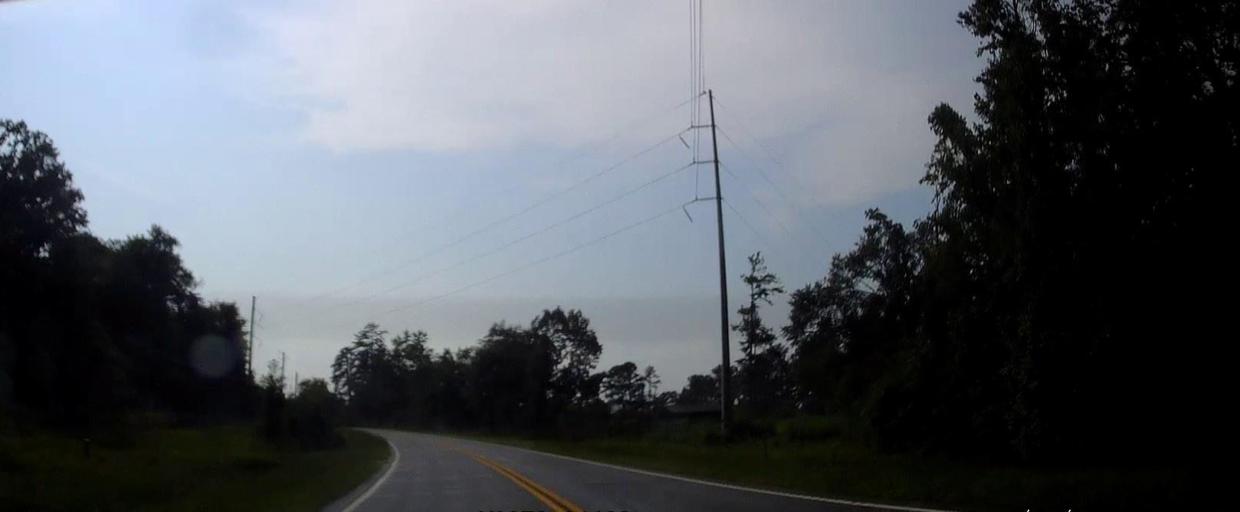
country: US
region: Georgia
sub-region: Twiggs County
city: Jeffersonville
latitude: 32.6002
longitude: -83.2387
